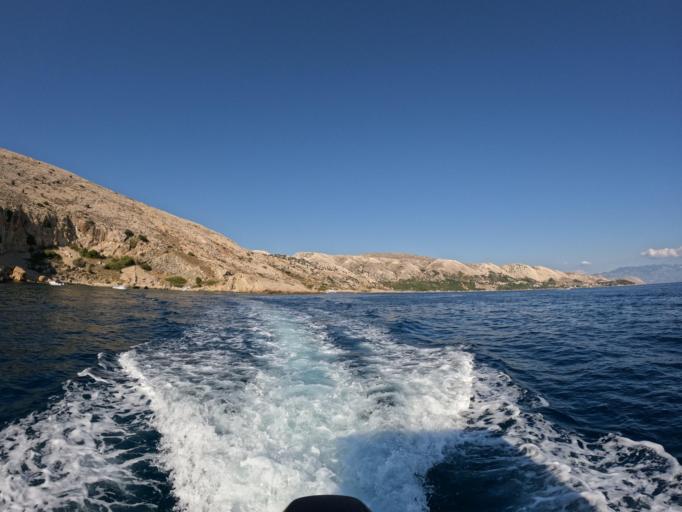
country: HR
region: Primorsko-Goranska
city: Punat
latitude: 44.9635
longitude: 14.6555
